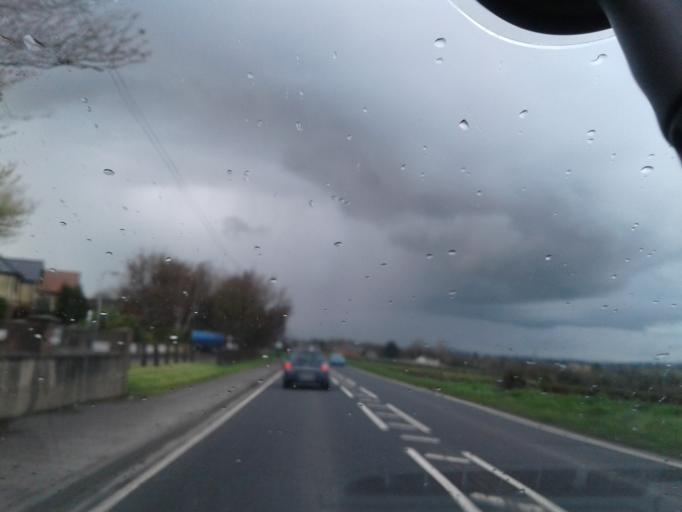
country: GB
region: Northern Ireland
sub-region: Strabane District
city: Sion Mills
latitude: 54.7763
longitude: -7.4669
